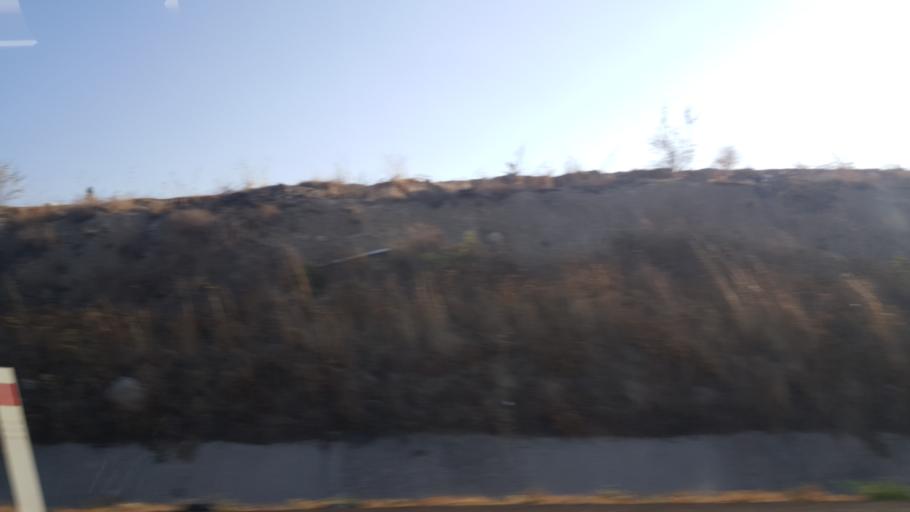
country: TR
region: Ankara
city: Polatli
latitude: 39.5742
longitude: 32.0233
